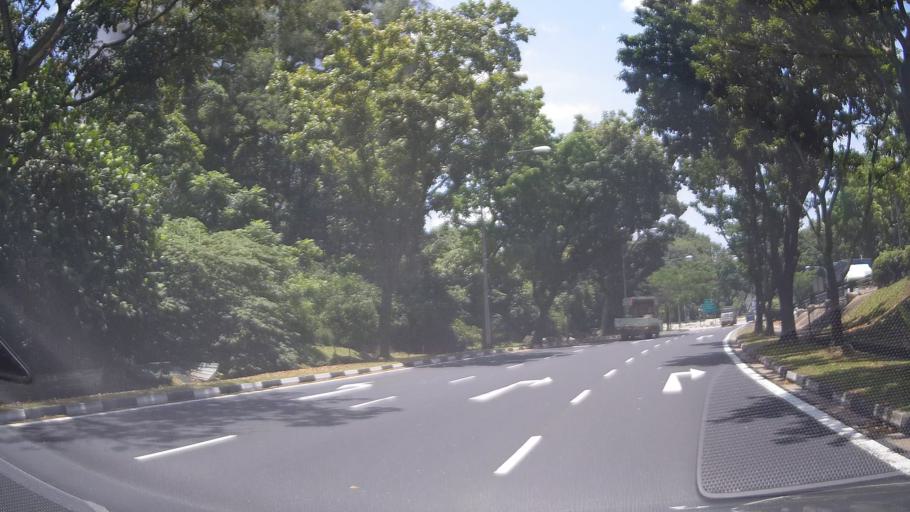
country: MY
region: Johor
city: Johor Bahru
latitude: 1.3878
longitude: 103.7577
